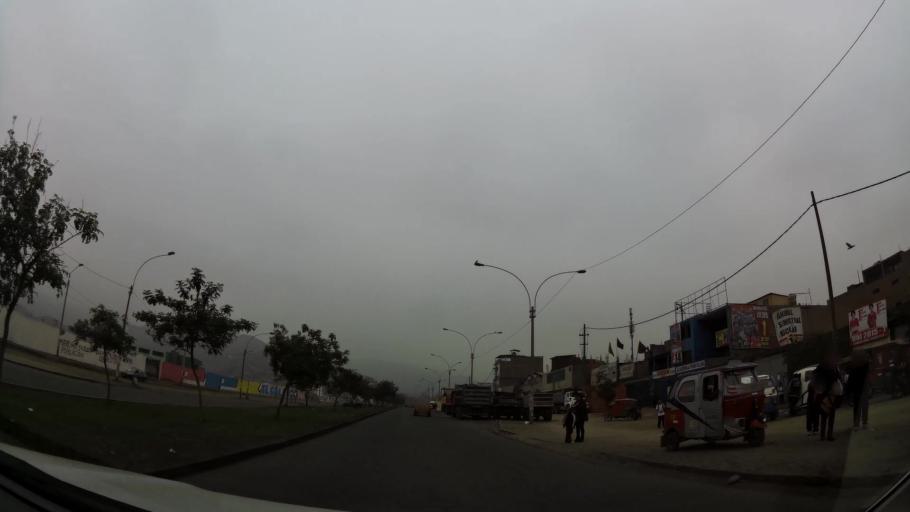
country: PE
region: Lima
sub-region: Lima
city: Independencia
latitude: -11.9558
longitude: -76.9858
